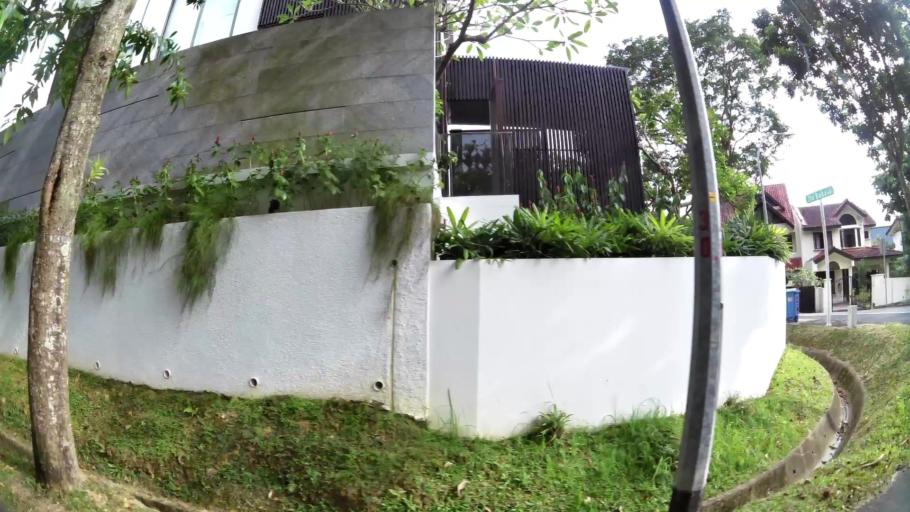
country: SG
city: Singapore
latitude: 1.3296
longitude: 103.8184
